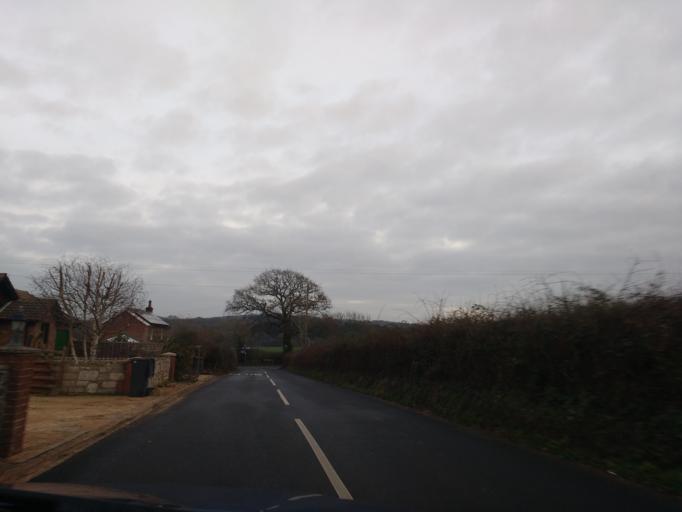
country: GB
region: England
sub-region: Isle of Wight
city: Northwood
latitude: 50.7250
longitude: -1.3551
